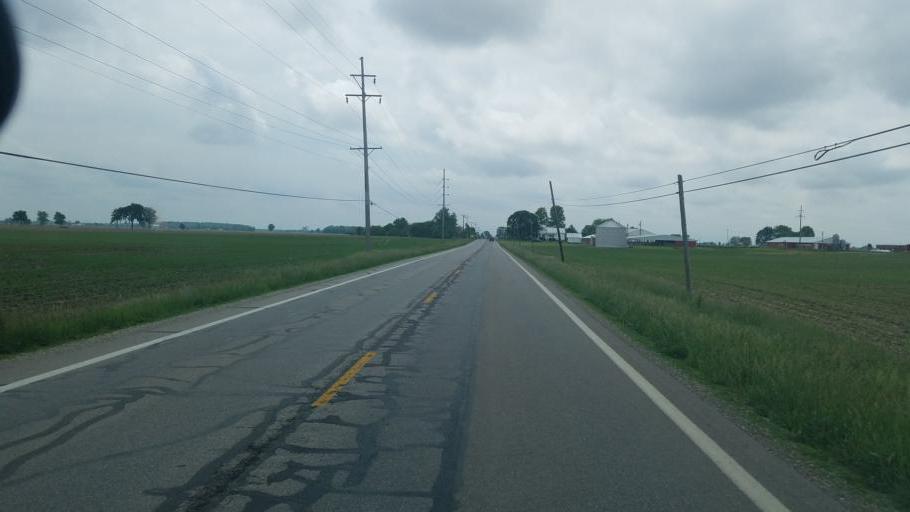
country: US
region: Ohio
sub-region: Marion County
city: Prospect
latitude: 40.4456
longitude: -83.2257
